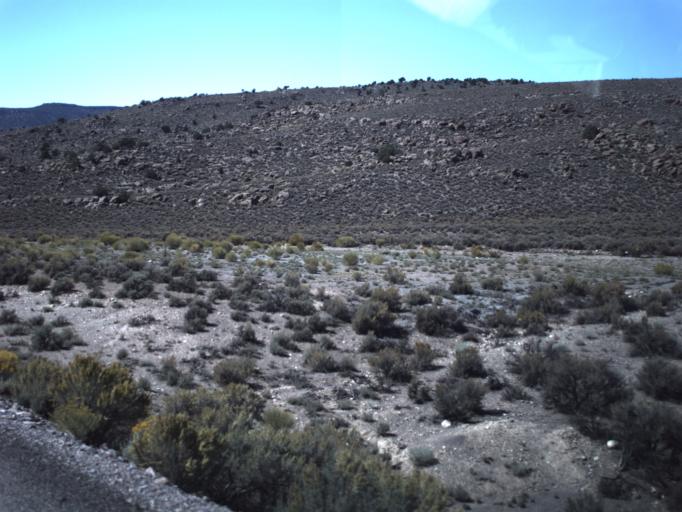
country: US
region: Utah
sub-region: Piute County
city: Junction
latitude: 38.1744
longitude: -112.0256
